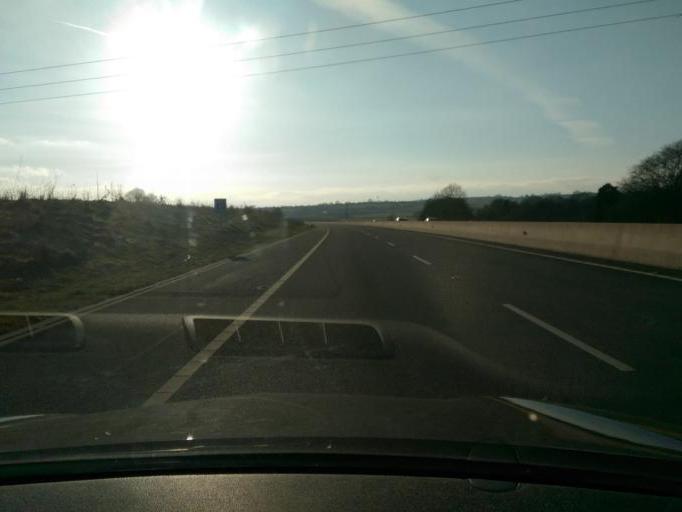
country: IE
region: Munster
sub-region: North Tipperary
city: Roscrea
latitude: 52.9271
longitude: -7.7672
